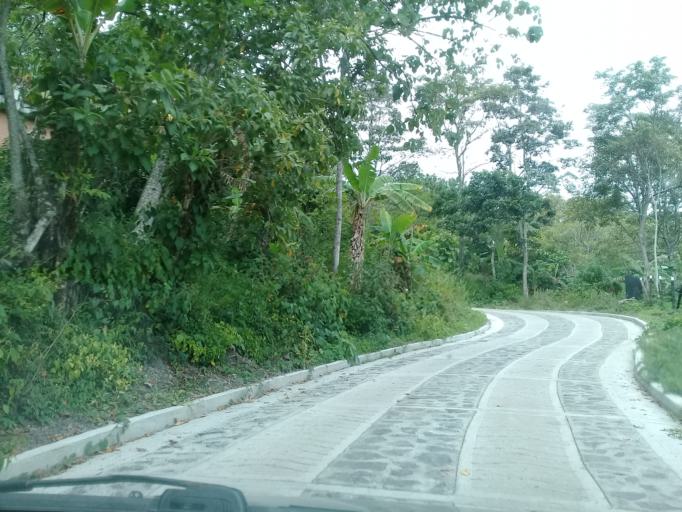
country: CO
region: Cundinamarca
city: Viani
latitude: 4.8685
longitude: -74.5389
